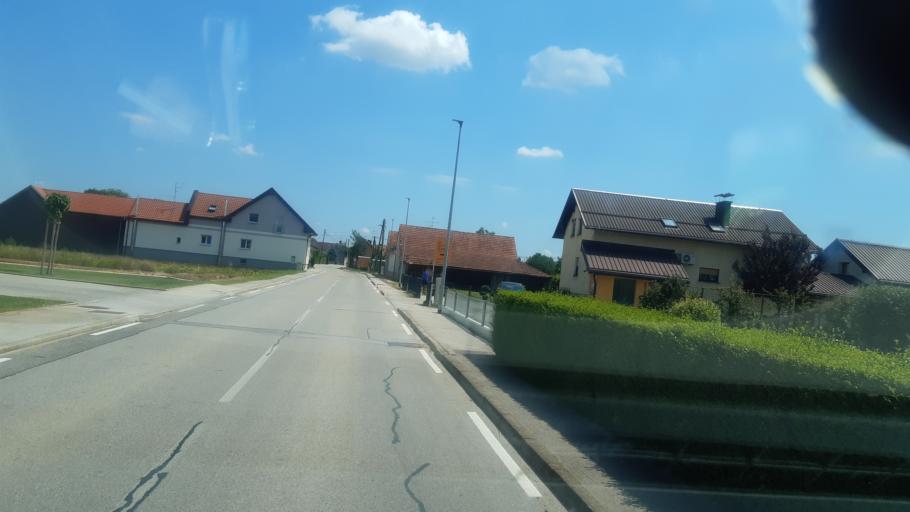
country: SI
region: Moravske Toplice
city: Moravske Toplice
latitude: 46.6697
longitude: 16.2187
